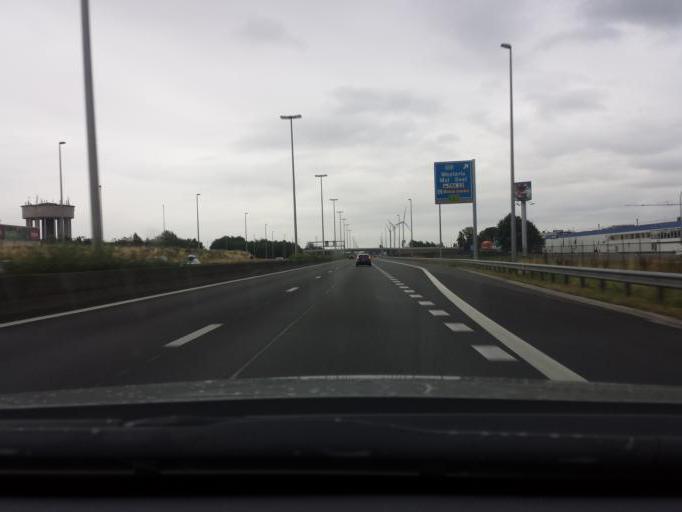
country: BE
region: Flanders
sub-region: Provincie Antwerpen
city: Westerlo
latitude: 51.1327
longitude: 4.9312
